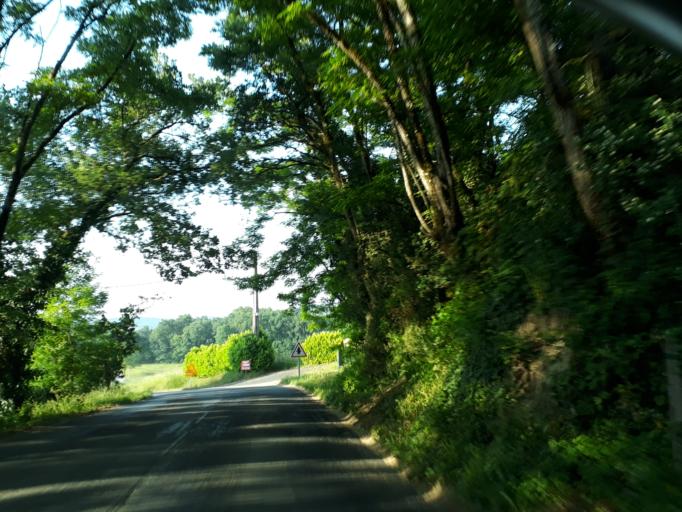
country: FR
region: Limousin
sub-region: Departement de la Correze
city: Saint-Pantaleon-de-Larche
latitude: 45.1064
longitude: 1.4670
